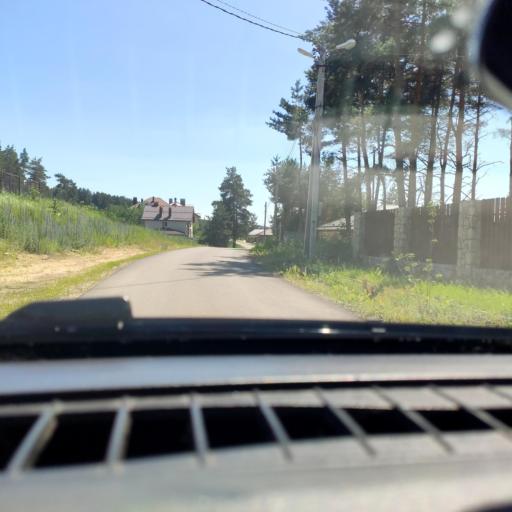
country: RU
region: Voronezj
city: Podgornoye
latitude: 51.7957
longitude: 39.1360
